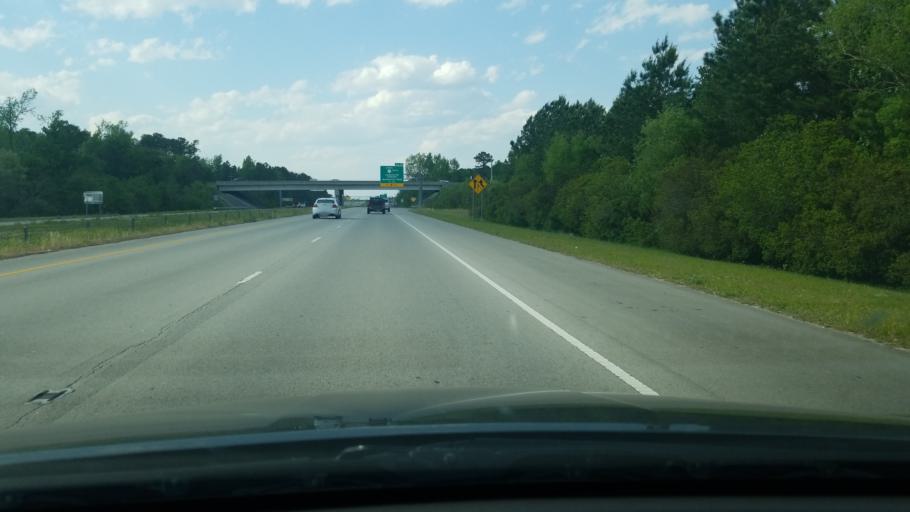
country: US
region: North Carolina
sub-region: Onslow County
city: Jacksonville
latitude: 34.7586
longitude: -77.3943
